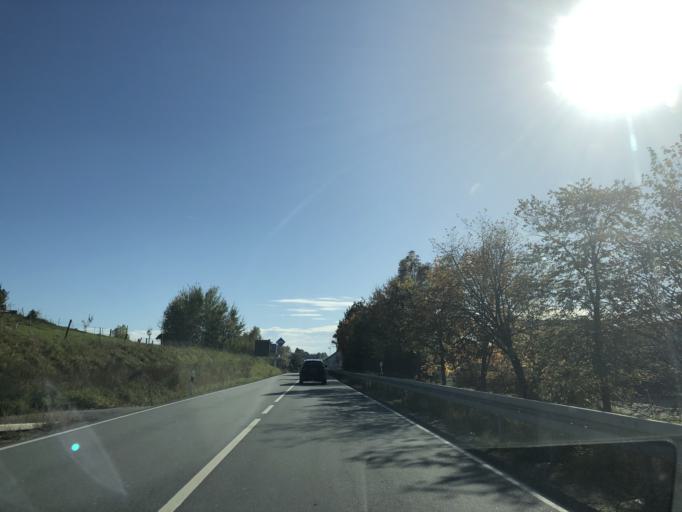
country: DE
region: Bavaria
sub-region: Lower Bavaria
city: Ruhmannsfelden
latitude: 48.9862
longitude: 12.9807
